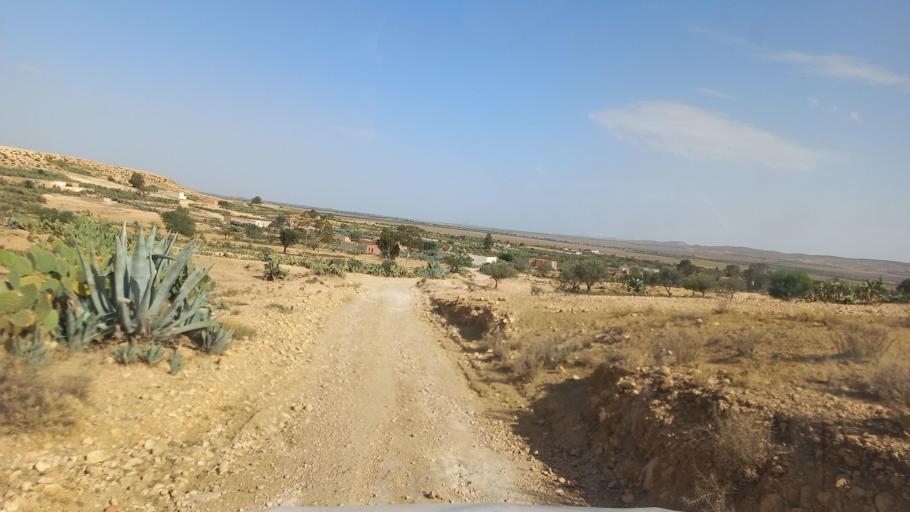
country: TN
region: Al Qasrayn
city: Kasserine
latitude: 35.2566
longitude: 8.9258
